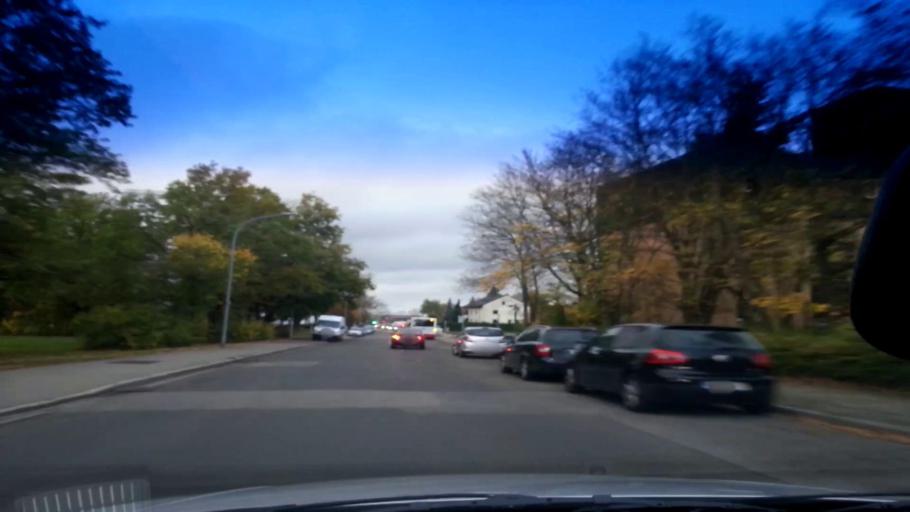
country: DE
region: Bavaria
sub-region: Upper Franconia
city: Bamberg
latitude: 49.9078
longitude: 10.9115
